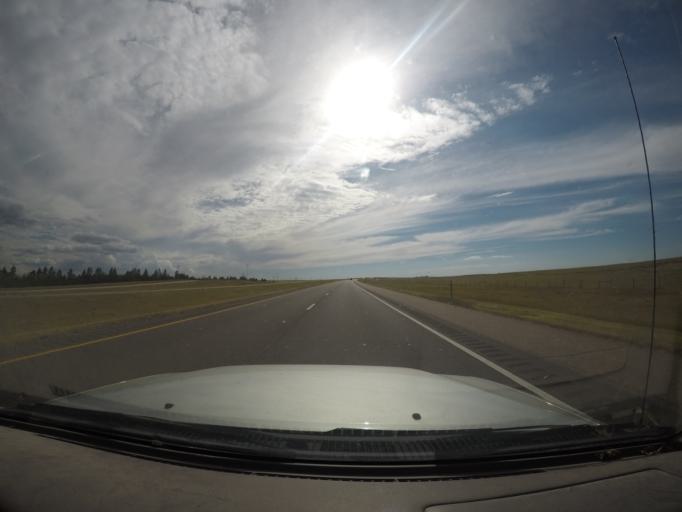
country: US
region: Nebraska
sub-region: Kimball County
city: Kimball
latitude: 41.1925
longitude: -103.7731
